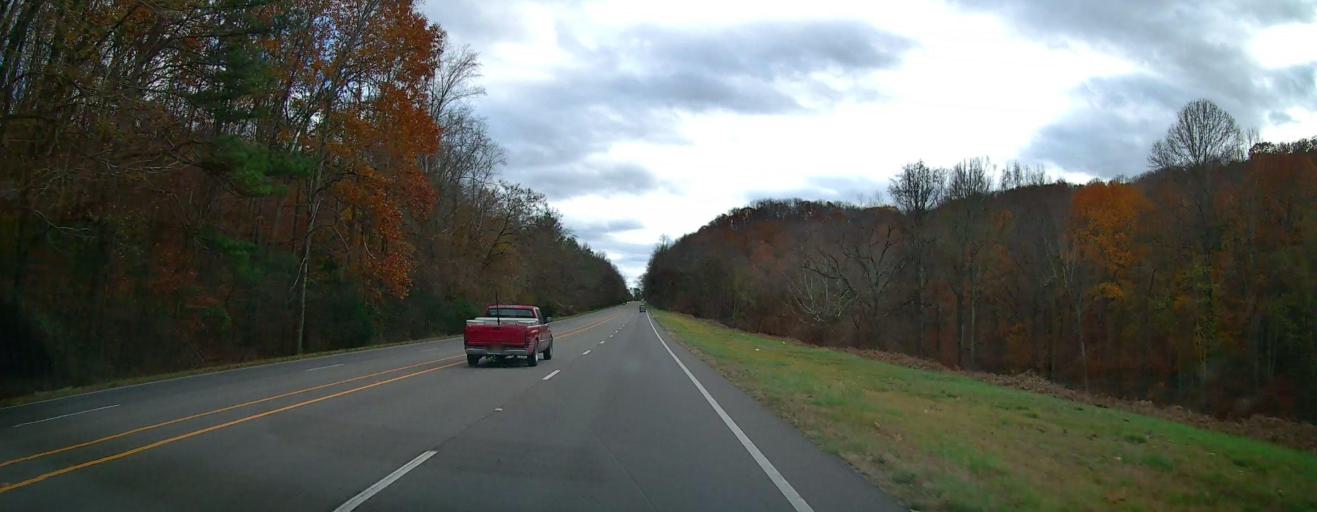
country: US
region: Alabama
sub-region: Morgan County
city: Falkville
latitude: 34.3175
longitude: -86.9999
